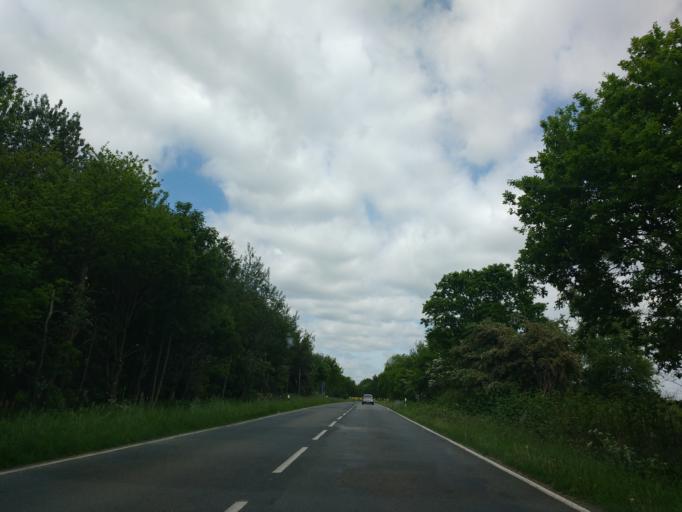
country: DE
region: Schleswig-Holstein
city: Braak
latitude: 53.5875
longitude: 10.2476
